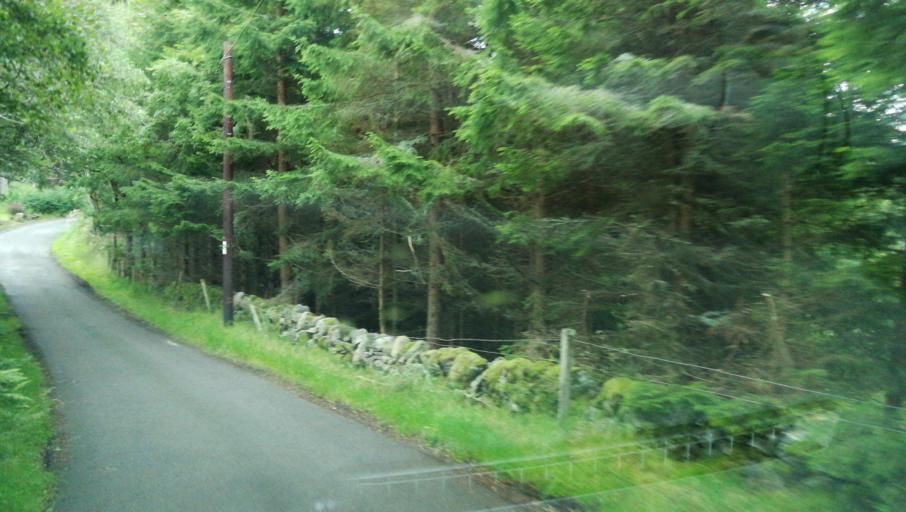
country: GB
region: Scotland
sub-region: Perth and Kinross
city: Blairgowrie
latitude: 56.6933
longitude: -3.4046
